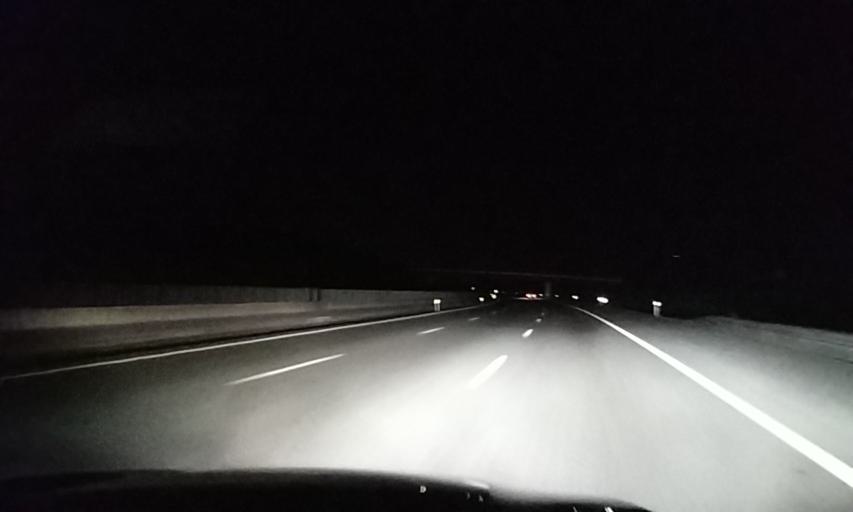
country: PT
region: Santarem
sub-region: Alcanena
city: Alcanena
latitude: 39.3769
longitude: -8.6298
